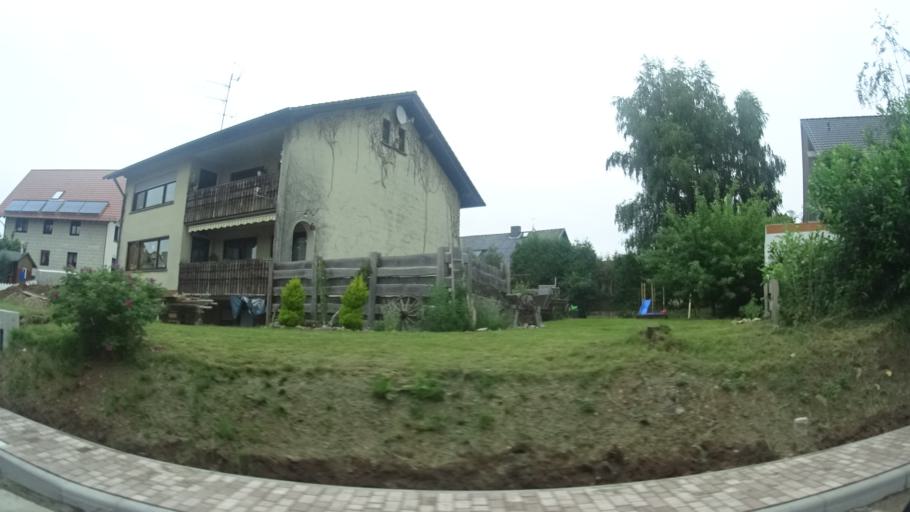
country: DE
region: Bavaria
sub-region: Regierungsbezirk Unterfranken
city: Krombach
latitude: 50.0854
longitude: 9.1886
